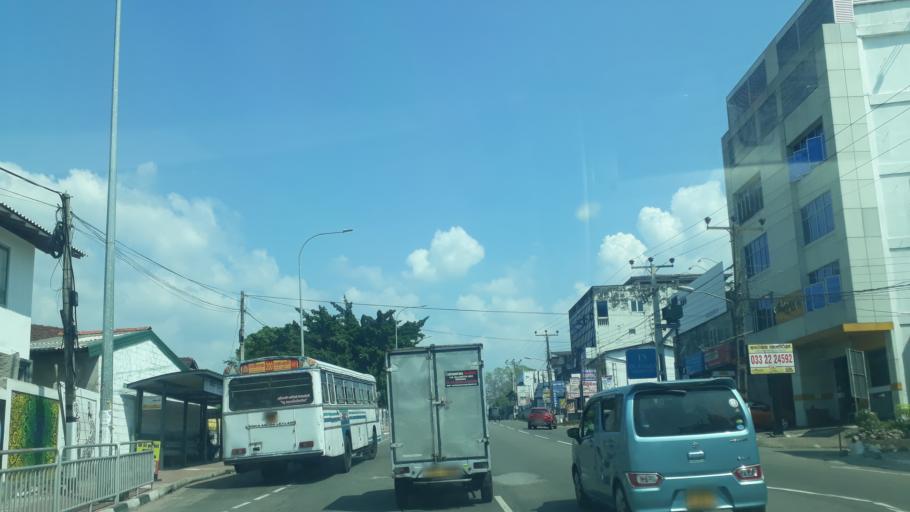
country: LK
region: Western
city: Gampaha
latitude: 7.0909
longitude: 80.0003
